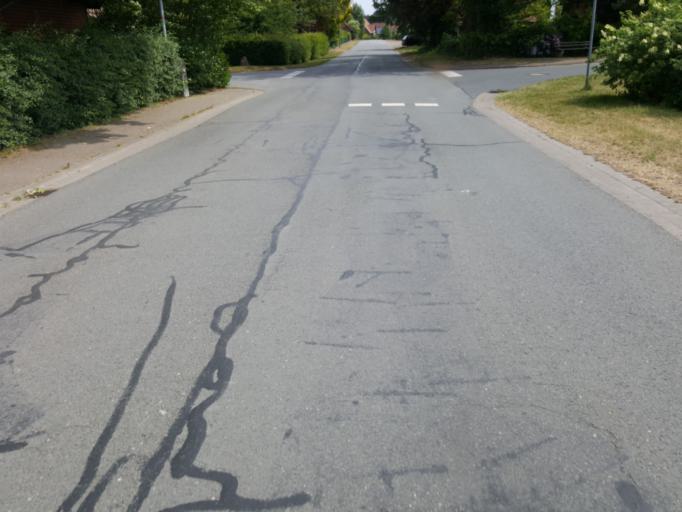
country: DE
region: Lower Saxony
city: Husum
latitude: 52.5650
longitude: 9.2525
